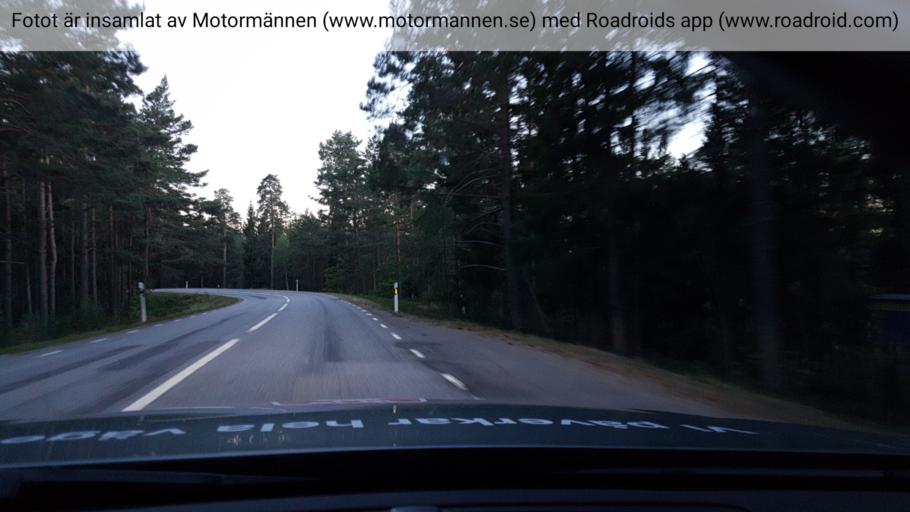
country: SE
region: Vaestmanland
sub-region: Hallstahammars Kommun
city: Hallstahammar
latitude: 59.6524
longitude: 16.1882
